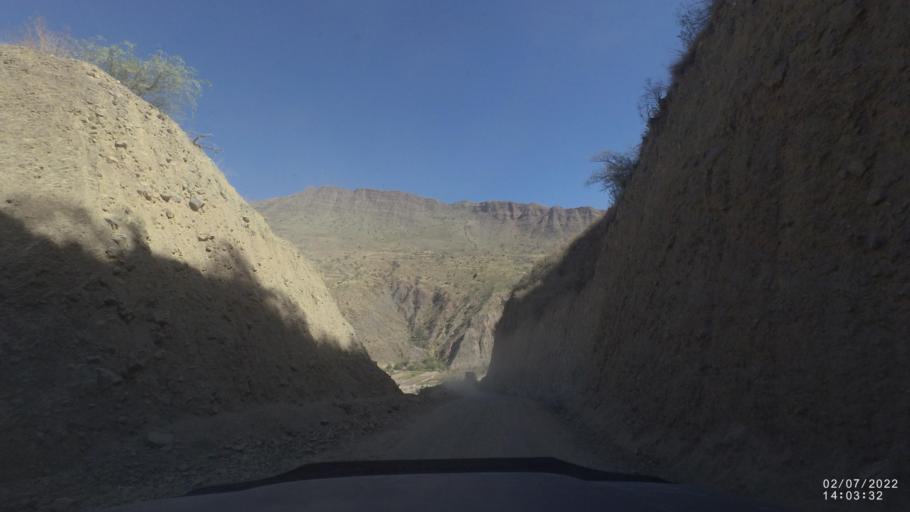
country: BO
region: Cochabamba
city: Irpa Irpa
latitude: -17.8231
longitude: -66.3911
